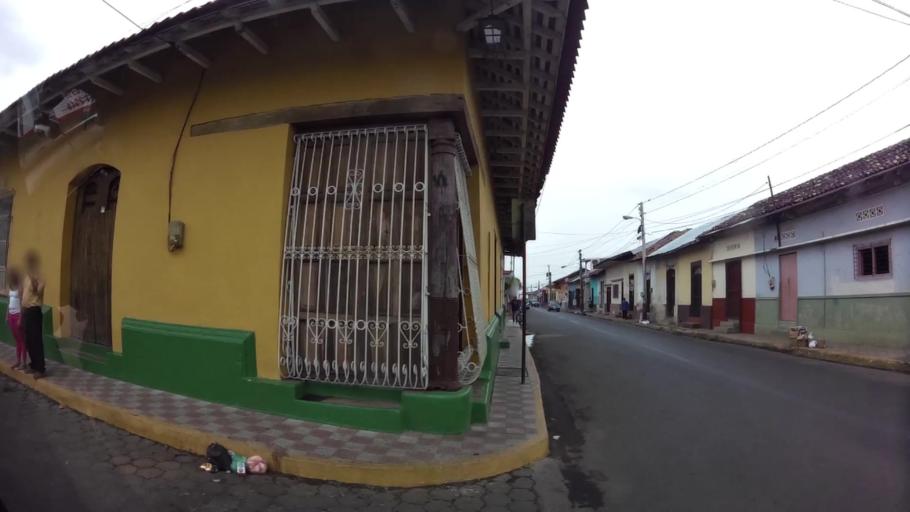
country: NI
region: Leon
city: Leon
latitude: 12.4424
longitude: -86.8760
